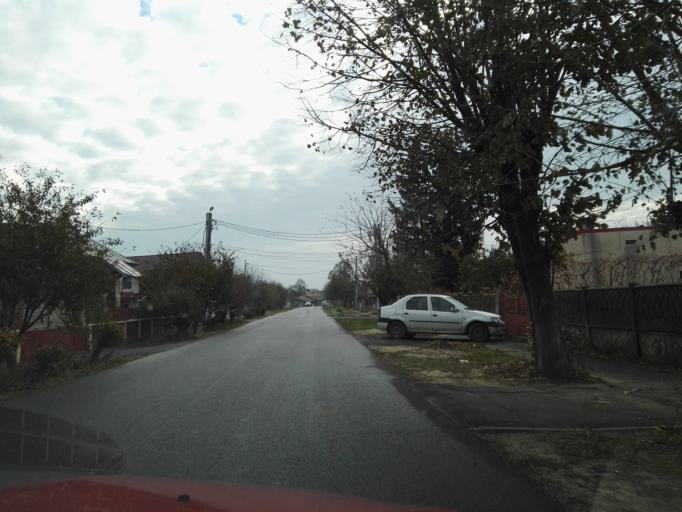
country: RO
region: Ilfov
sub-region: Comuna Magurele
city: Alunisu
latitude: 44.3375
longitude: 26.0596
